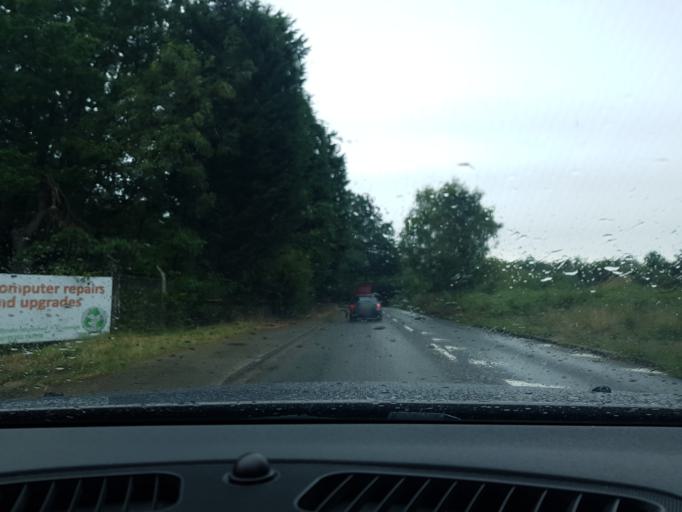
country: GB
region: England
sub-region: Surrey
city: Farnham
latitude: 51.2353
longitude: -0.8149
